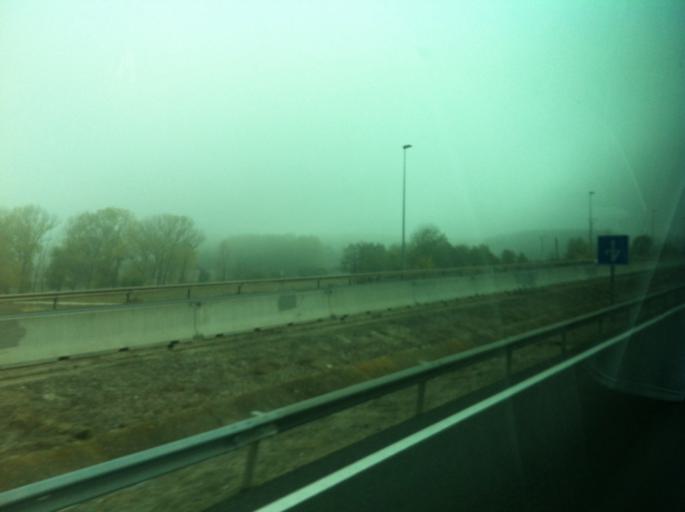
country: ES
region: Castille and Leon
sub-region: Provincia de Burgos
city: Saldana de Burgos
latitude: 42.2727
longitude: -3.7015
